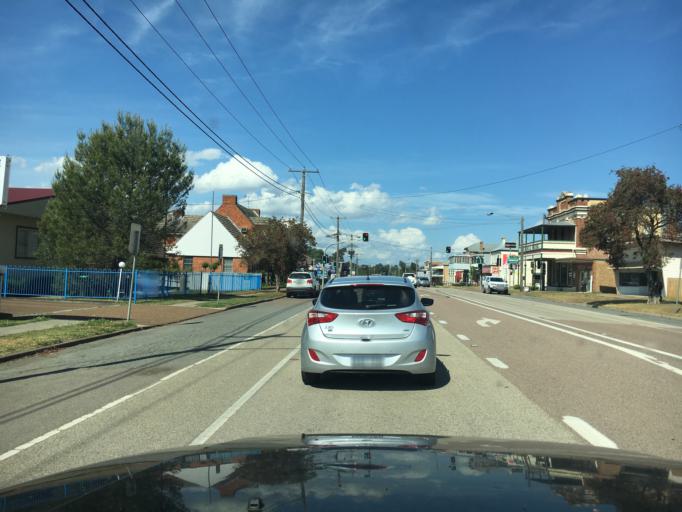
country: AU
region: New South Wales
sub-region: Cessnock
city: Branxton
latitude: -32.6559
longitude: 151.3504
